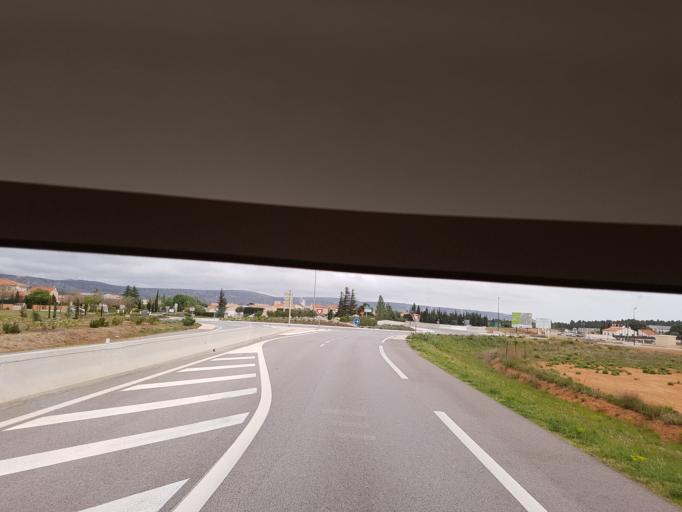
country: FR
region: Languedoc-Roussillon
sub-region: Departement des Pyrenees-Orientales
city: Salses-le-Chateau
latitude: 42.8225
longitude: 2.9169
